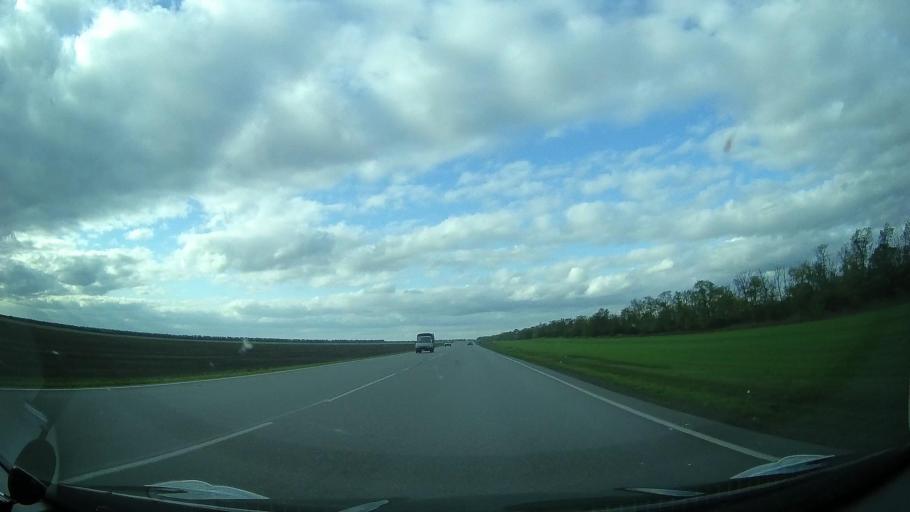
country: RU
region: Rostov
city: Kagal'nitskaya
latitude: 46.8996
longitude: 40.1240
